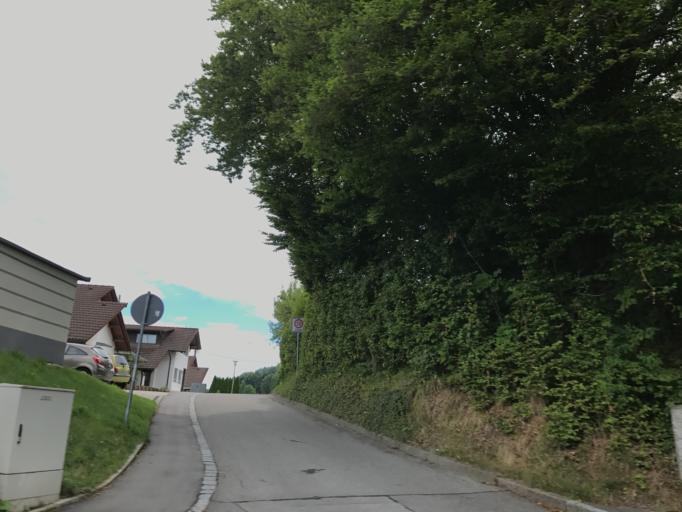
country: DE
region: Baden-Wuerttemberg
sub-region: Tuebingen Region
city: Berg
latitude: 47.8523
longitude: 9.6020
